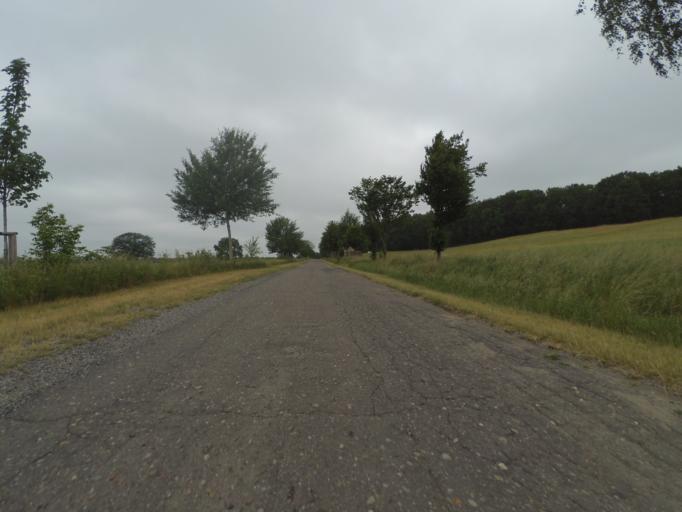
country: DE
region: Mecklenburg-Vorpommern
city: Plau am See
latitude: 53.4832
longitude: 12.2297
